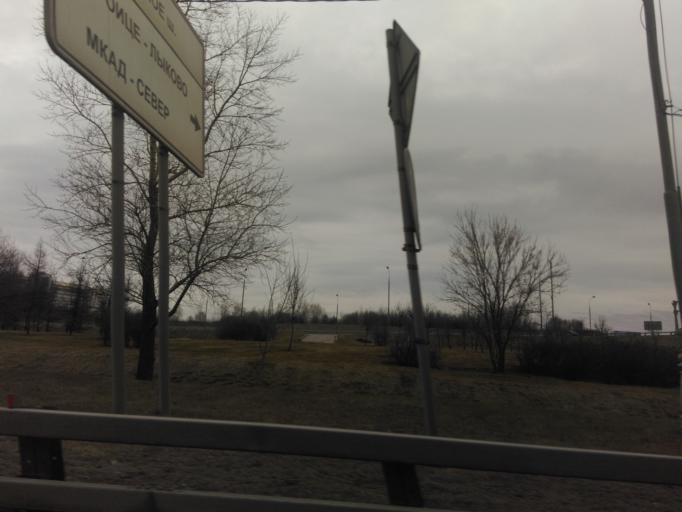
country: RU
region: Moscow
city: Rublevo
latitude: 55.7652
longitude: 37.3701
